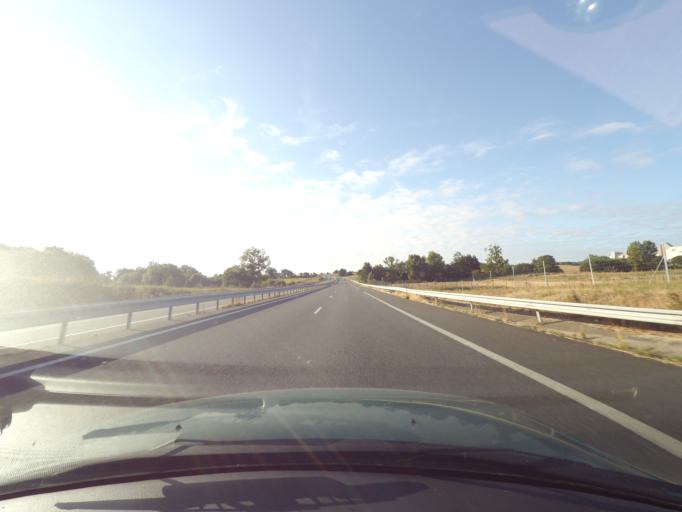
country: FR
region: Poitou-Charentes
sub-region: Departement des Deux-Sevres
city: Combrand
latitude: 46.9122
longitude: -0.6829
